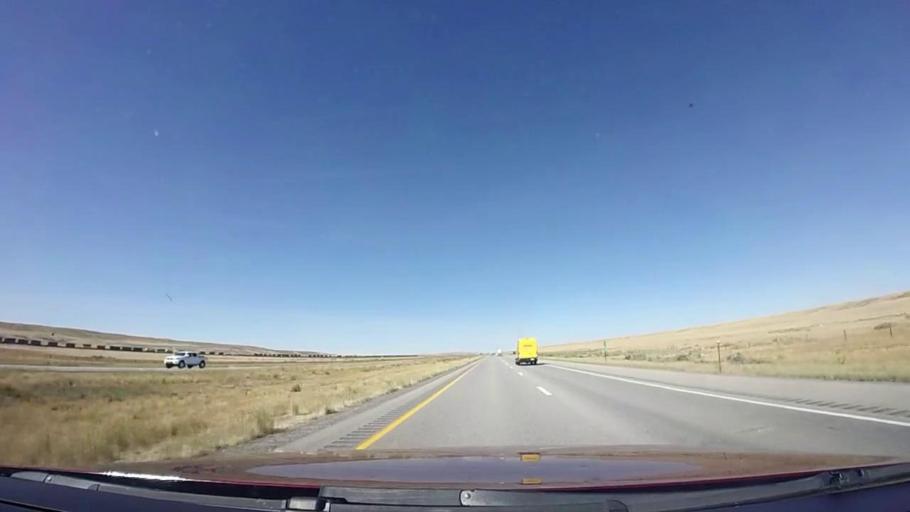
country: US
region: Wyoming
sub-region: Carbon County
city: Rawlins
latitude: 41.6588
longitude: -108.0820
